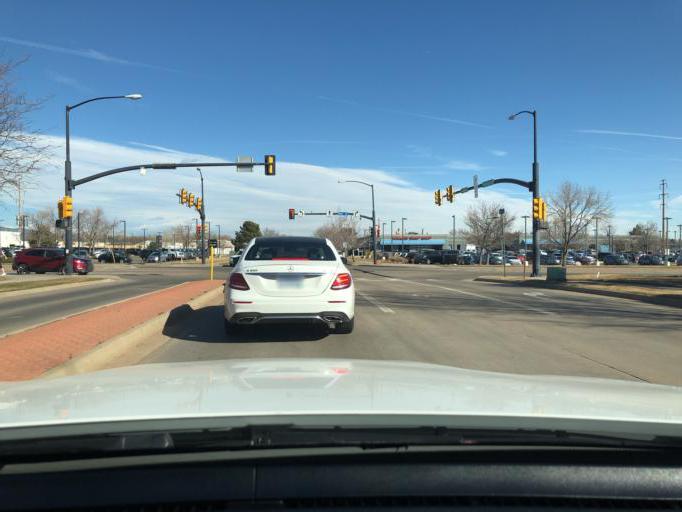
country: US
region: Colorado
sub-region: Boulder County
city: Boulder
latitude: 40.0216
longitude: -105.2385
